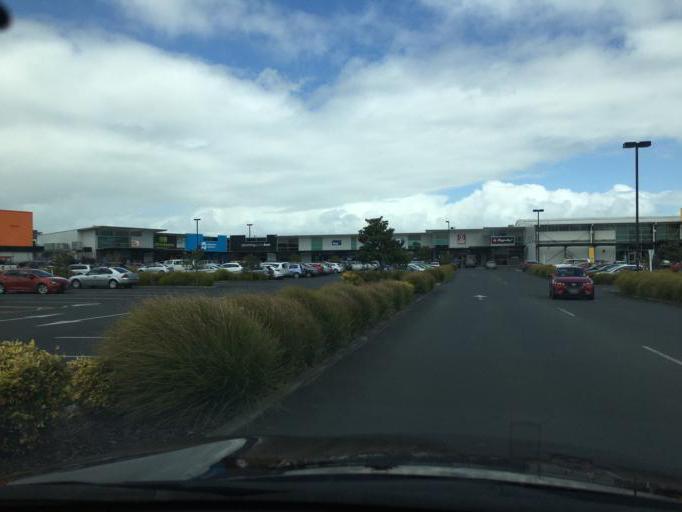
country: NZ
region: Waikato
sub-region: Waipa District
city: Cambridge
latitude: -38.0070
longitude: 175.3400
